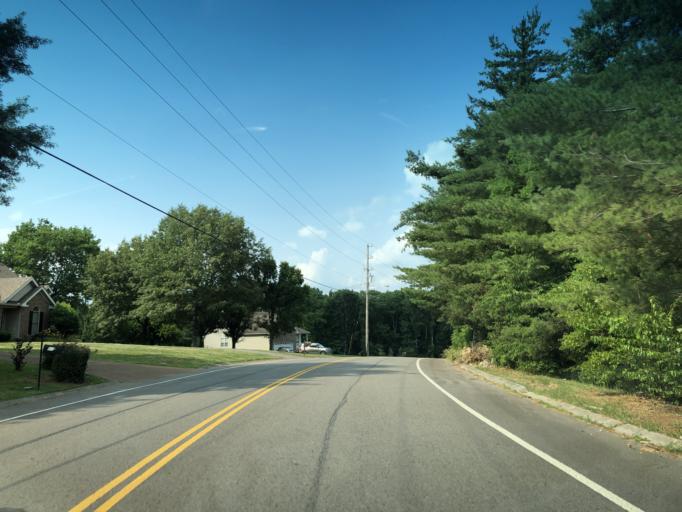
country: US
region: Tennessee
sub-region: Davidson County
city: Goodlettsville
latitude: 36.2710
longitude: -86.7238
